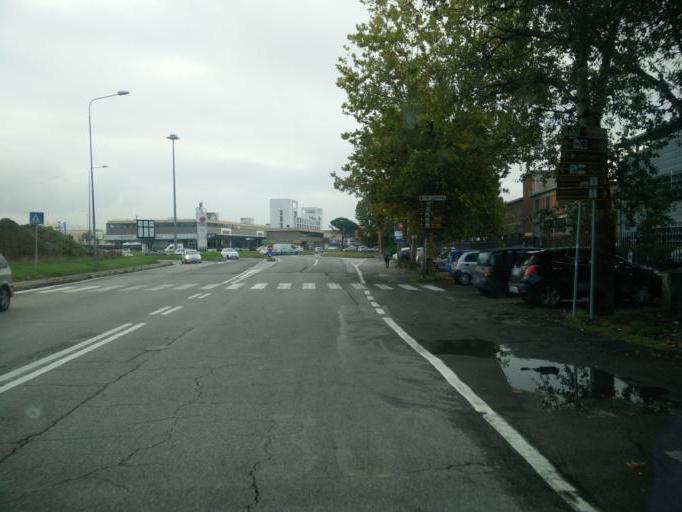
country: IT
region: Tuscany
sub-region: Province of Florence
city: Mantignano-Ugnano
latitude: 43.8072
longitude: 11.1763
